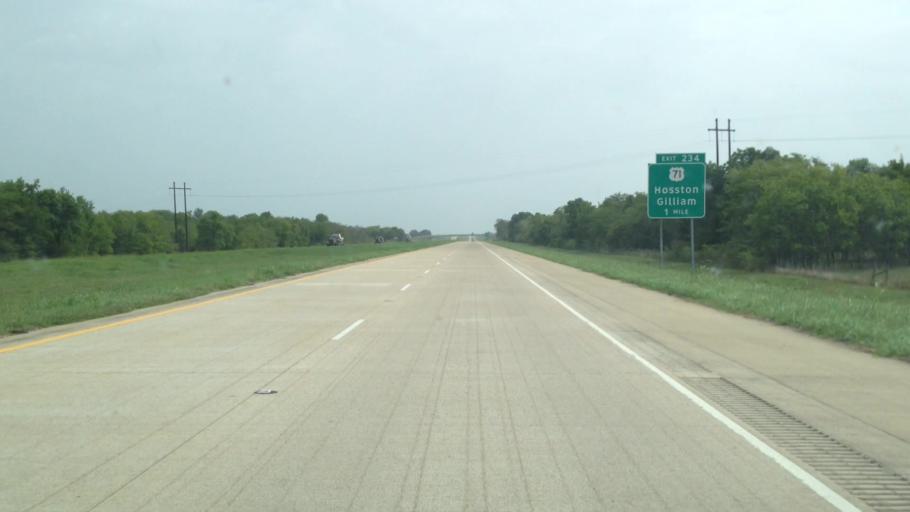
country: US
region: Louisiana
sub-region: Caddo Parish
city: Vivian
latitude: 32.8329
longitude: -93.8737
